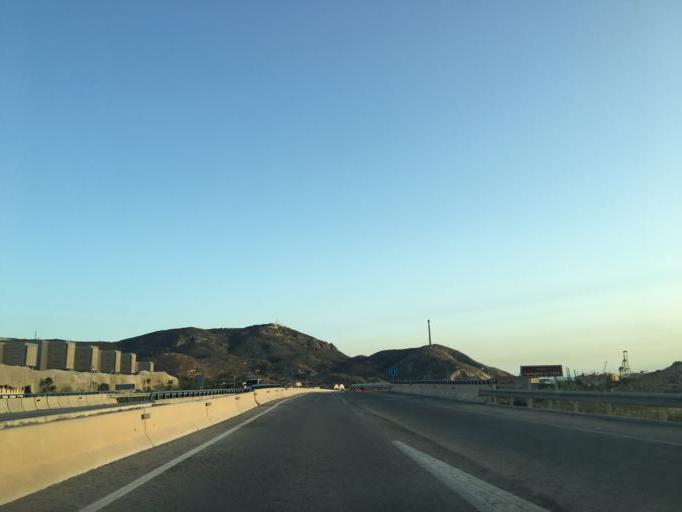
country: ES
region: Murcia
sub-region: Murcia
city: Cartagena
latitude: 37.6049
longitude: -0.9620
